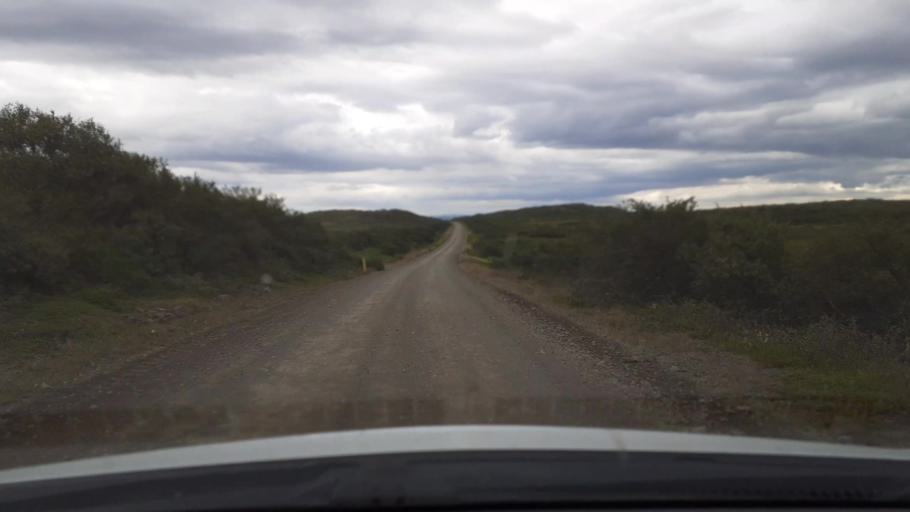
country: IS
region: West
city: Borgarnes
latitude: 64.5978
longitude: -21.9793
